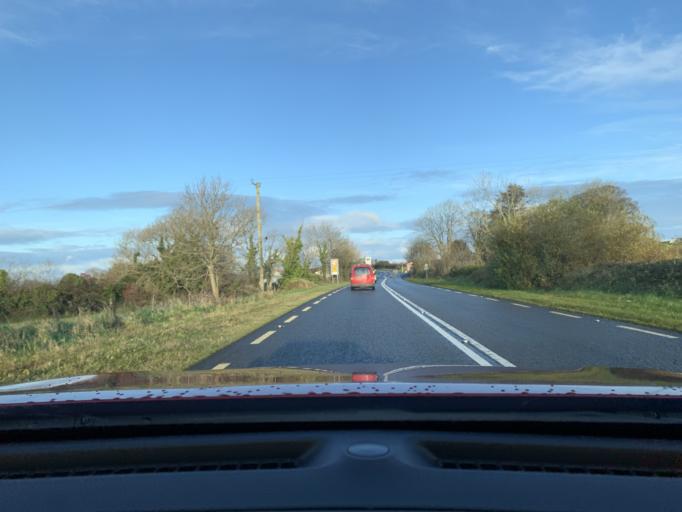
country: IE
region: Connaught
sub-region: Sligo
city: Sligo
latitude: 54.3585
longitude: -8.5208
